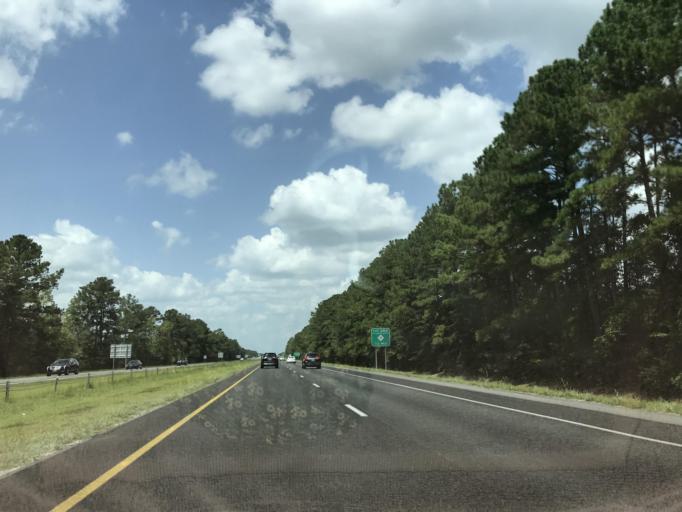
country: US
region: North Carolina
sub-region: Duplin County
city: Wallace
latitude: 34.7604
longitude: -77.9558
